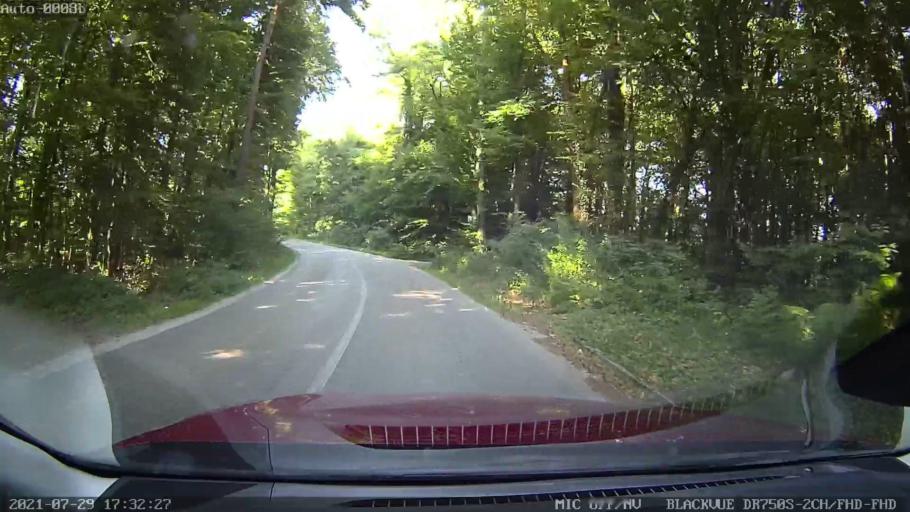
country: HR
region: Varazdinska
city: Vinica
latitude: 46.2919
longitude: 16.1312
